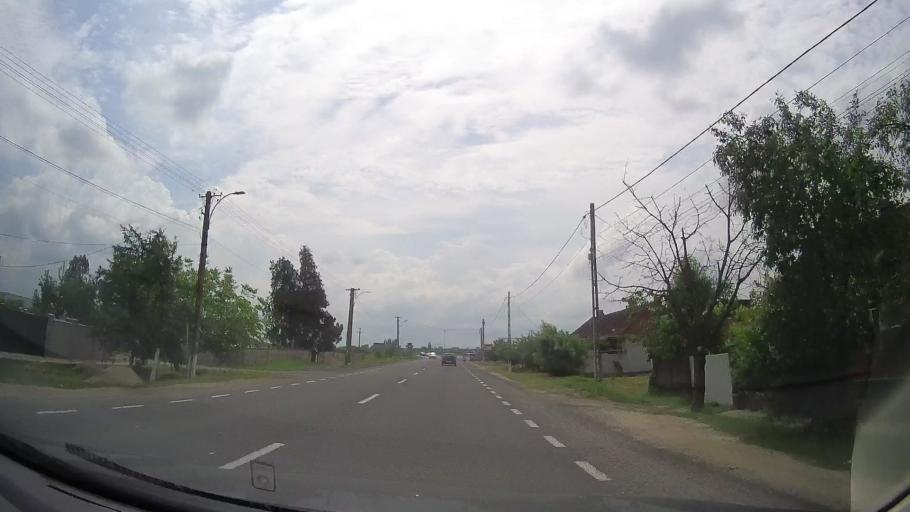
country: RO
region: Timis
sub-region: Comuna Costeiu
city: Costeiu
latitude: 45.7290
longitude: 21.8692
